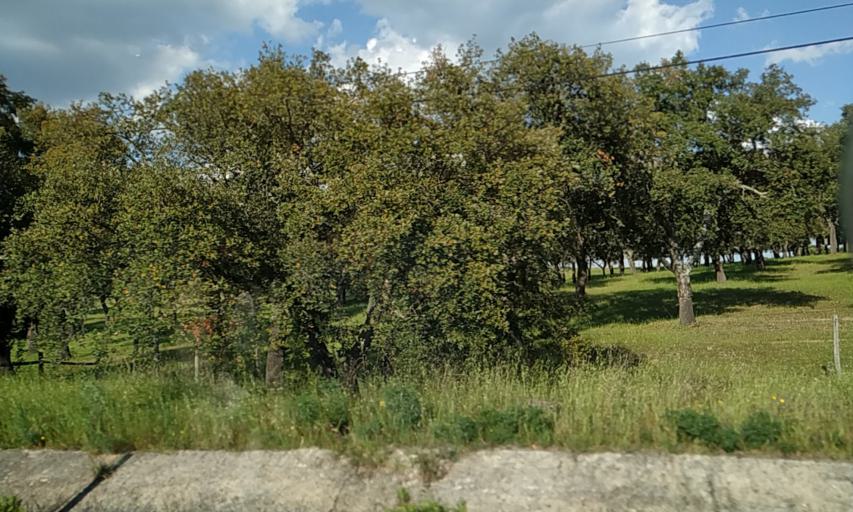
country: PT
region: Portalegre
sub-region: Portalegre
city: Urra
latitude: 39.1914
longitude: -7.4567
